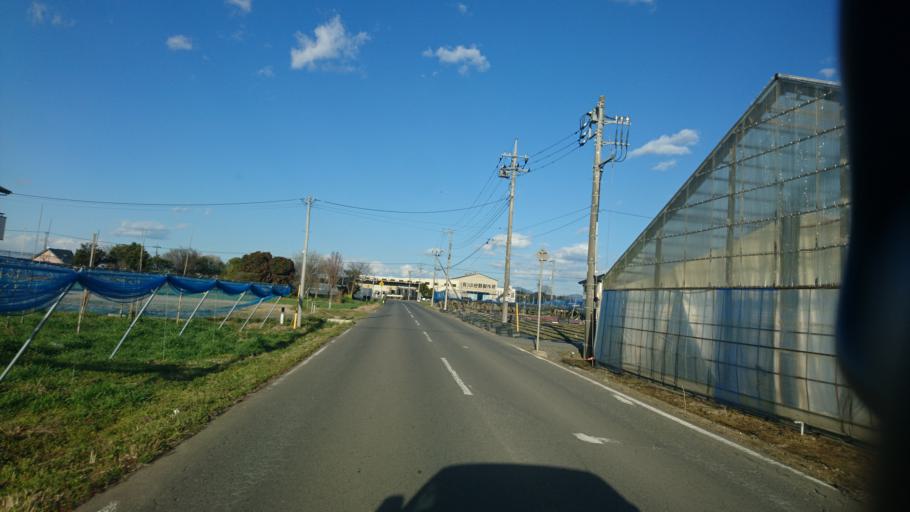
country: JP
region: Ibaraki
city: Yuki
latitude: 36.2617
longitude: 139.9190
